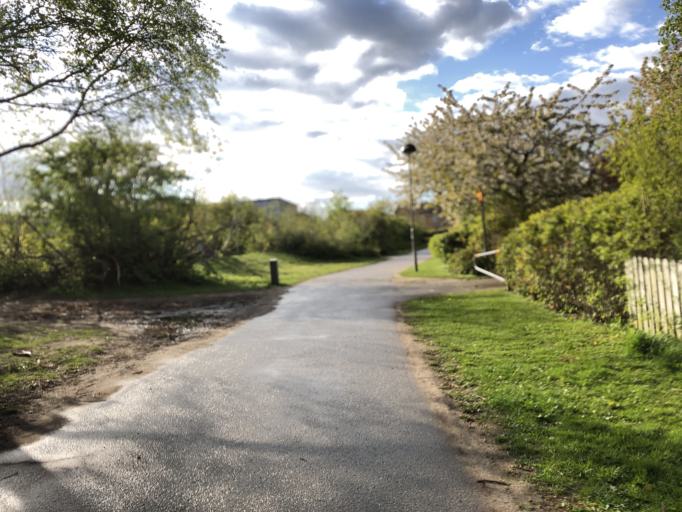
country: SE
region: Skane
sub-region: Lunds Kommun
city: Lund
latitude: 55.7101
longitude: 13.2412
